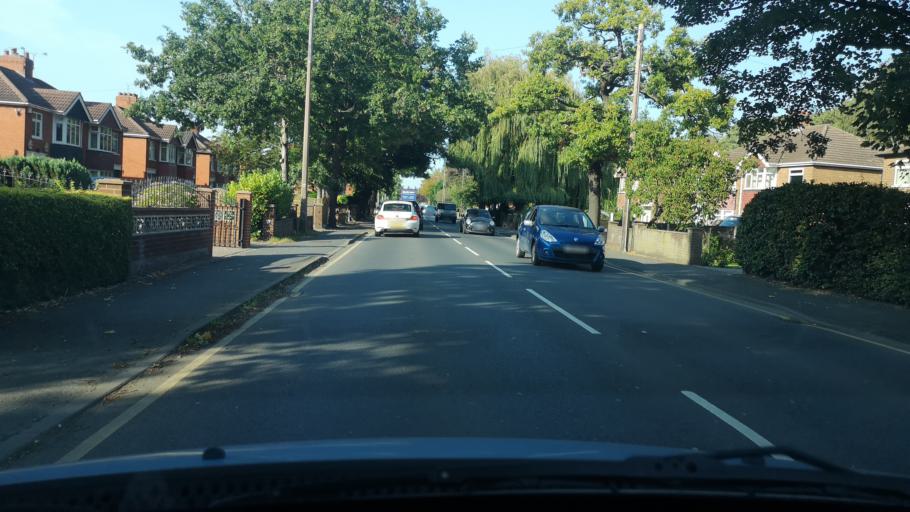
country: GB
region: England
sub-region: North Lincolnshire
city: Scunthorpe
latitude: 53.5874
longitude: -0.6840
